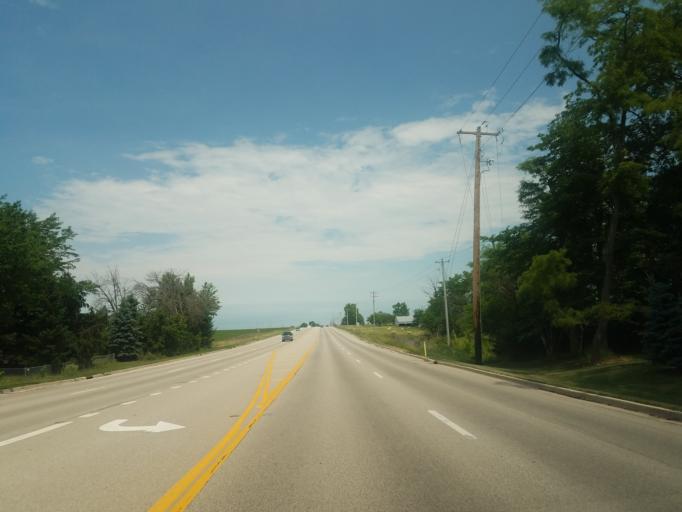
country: US
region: Illinois
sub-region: McLean County
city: Downs
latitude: 40.4251
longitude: -88.9014
